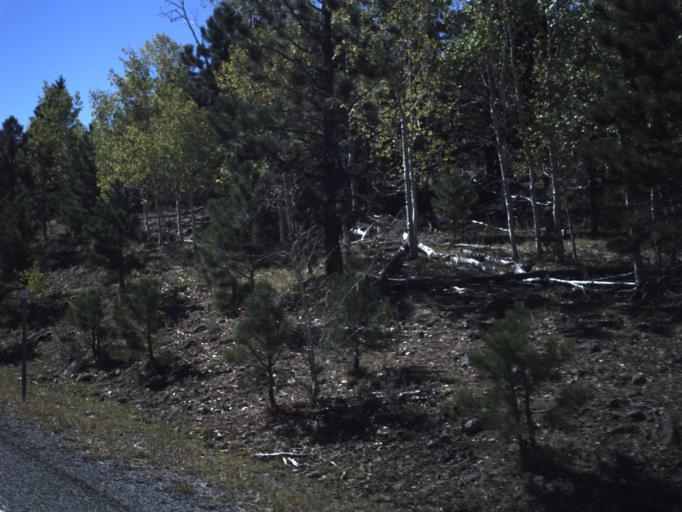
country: US
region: Utah
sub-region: Wayne County
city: Loa
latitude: 38.1289
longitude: -111.3286
